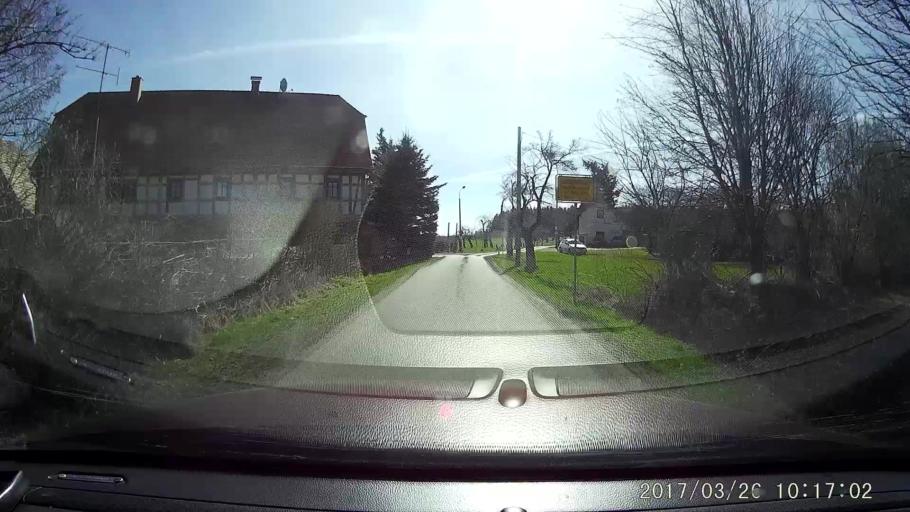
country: DE
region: Saxony
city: Herrnhut
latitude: 51.0630
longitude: 14.7595
